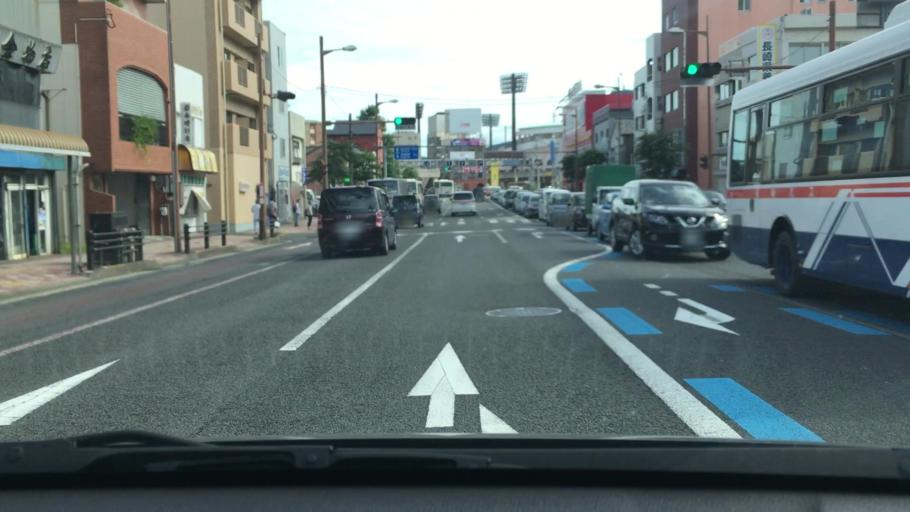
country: JP
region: Nagasaki
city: Nagasaki-shi
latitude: 32.7802
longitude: 129.8622
